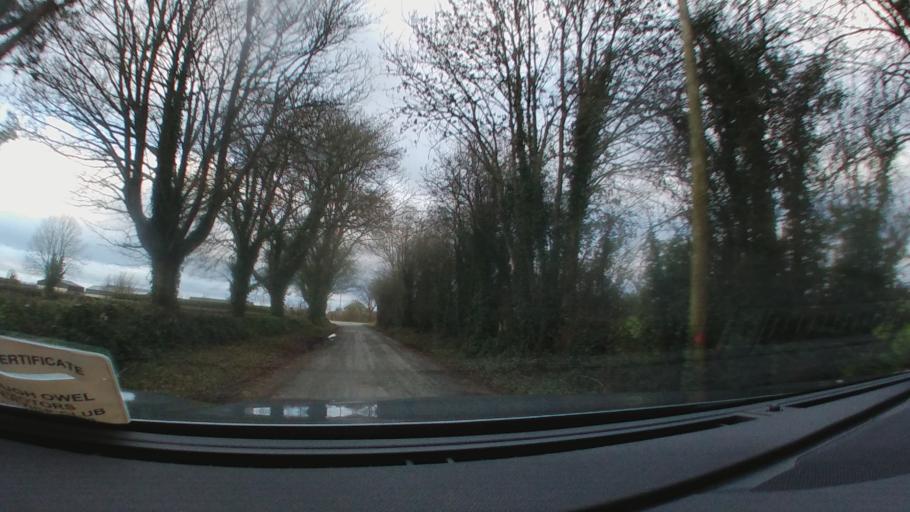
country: IE
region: Leinster
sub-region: Kilkenny
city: Thomastown
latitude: 52.5679
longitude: -7.1454
